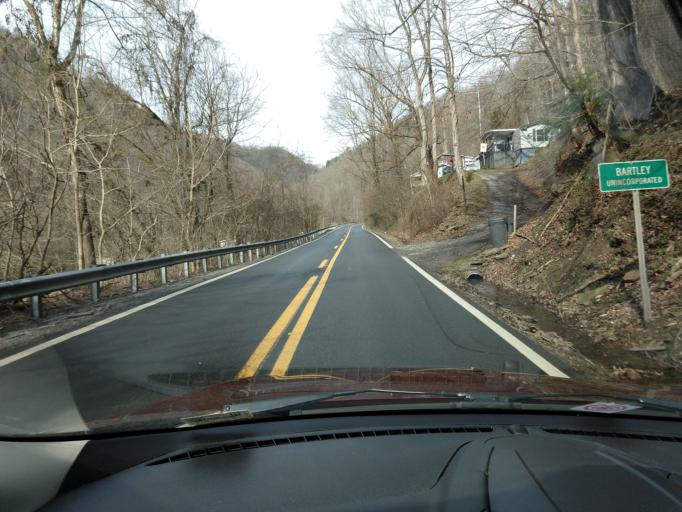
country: US
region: West Virginia
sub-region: McDowell County
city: Welch
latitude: 37.3429
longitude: -81.7397
